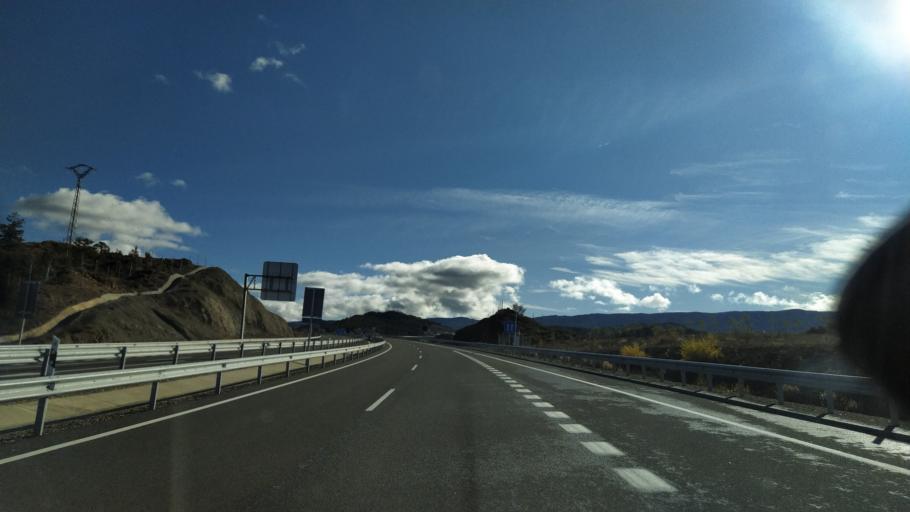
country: ES
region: Aragon
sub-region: Provincia de Huesca
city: Arguis
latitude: 42.4099
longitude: -0.3893
